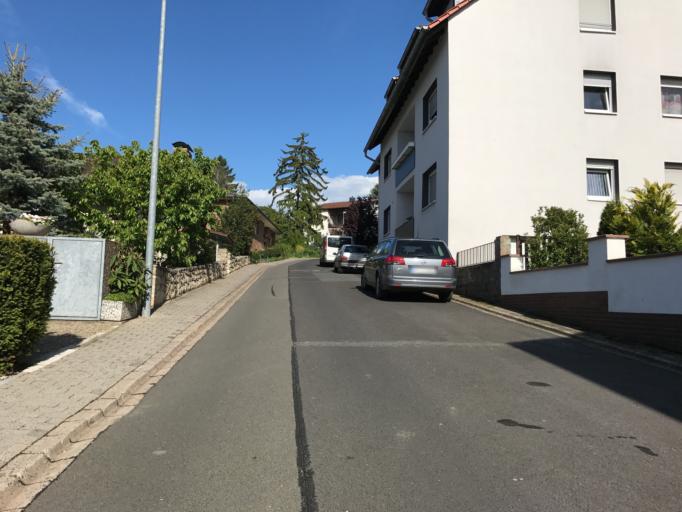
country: DE
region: Rheinland-Pfalz
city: Wackernheim
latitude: 49.9790
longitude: 8.1210
